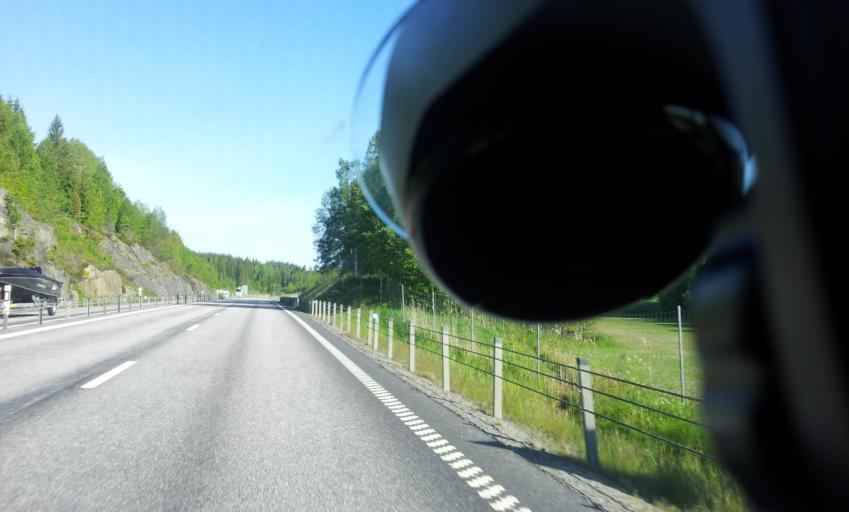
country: SE
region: OEstergoetland
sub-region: Valdemarsviks Kommun
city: Gusum
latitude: 58.2854
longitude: 16.5030
